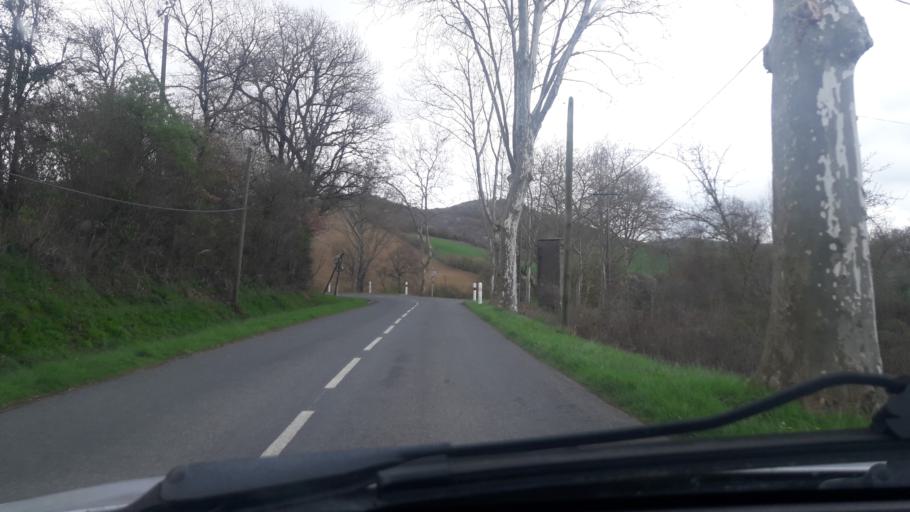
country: FR
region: Midi-Pyrenees
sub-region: Departement de la Haute-Garonne
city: Montesquieu-Volvestre
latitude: 43.2319
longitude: 1.2836
